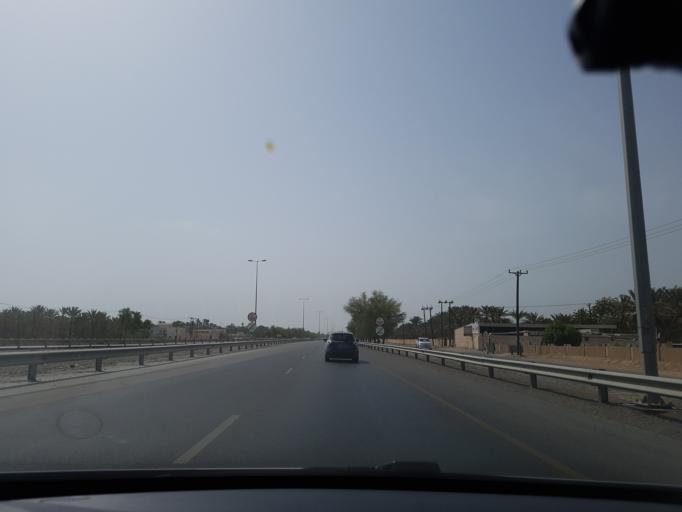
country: OM
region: Al Batinah
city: Al Khaburah
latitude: 23.9593
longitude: 57.1003
